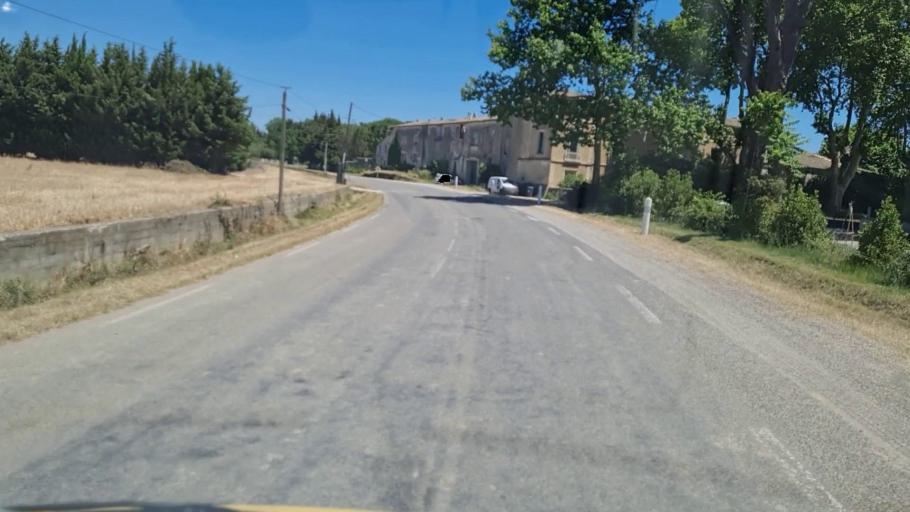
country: FR
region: Languedoc-Roussillon
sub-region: Departement de l'Herault
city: Marsillargues
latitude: 43.6887
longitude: 4.1763
